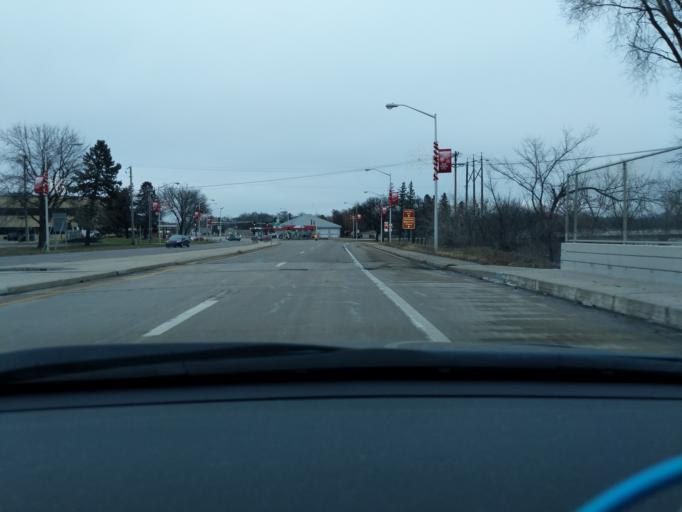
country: US
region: Minnesota
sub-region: Yellow Medicine County
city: Granite Falls
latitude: 44.8041
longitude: -95.5464
